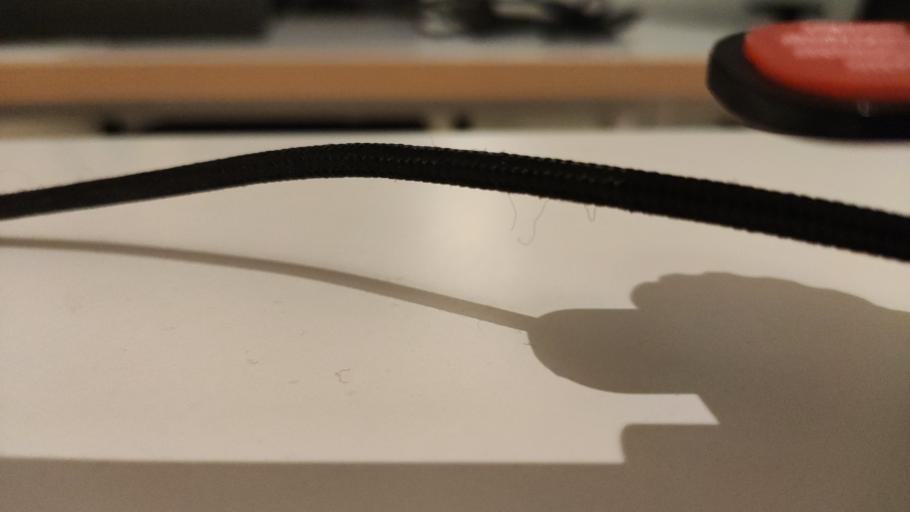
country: RU
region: Moskovskaya
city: Skoropuskovskiy
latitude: 56.3760
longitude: 38.1028
